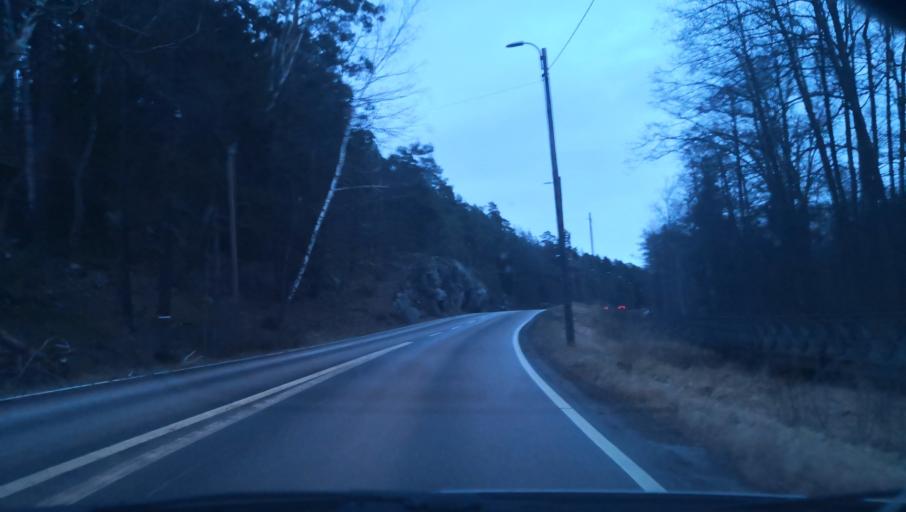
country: SE
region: Stockholm
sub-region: Varmdo Kommun
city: Gustavsberg
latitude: 59.3316
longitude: 18.3483
